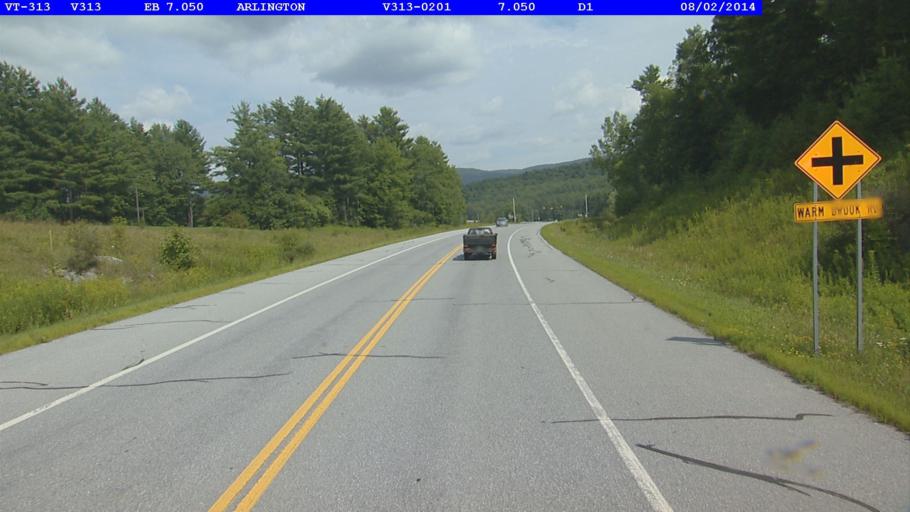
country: US
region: Vermont
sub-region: Bennington County
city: Arlington
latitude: 43.0549
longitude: -73.1550
